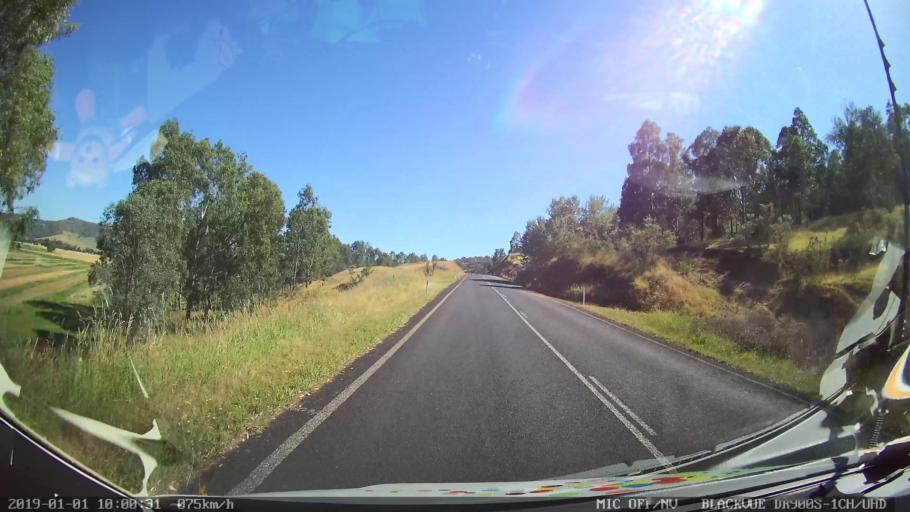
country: AU
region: New South Wales
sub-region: Snowy River
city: Jindabyne
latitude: -36.2013
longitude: 148.1019
